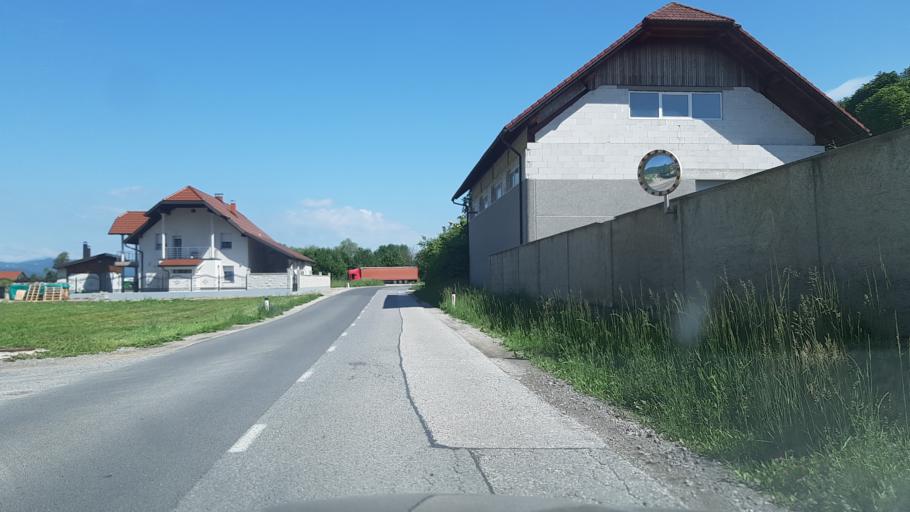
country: SI
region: Borovnica
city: Borovnica
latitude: 45.9332
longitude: 14.3627
